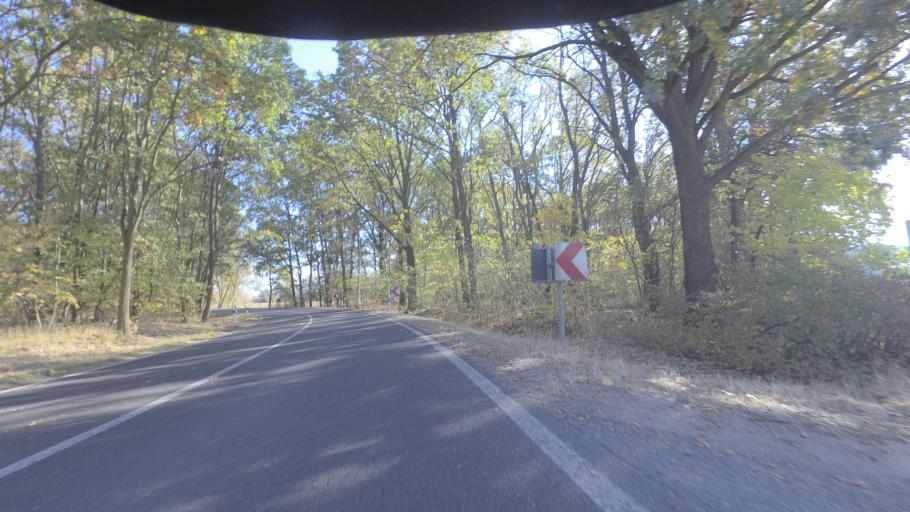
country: DE
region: Brandenburg
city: Zossen
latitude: 52.2539
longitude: 13.4623
